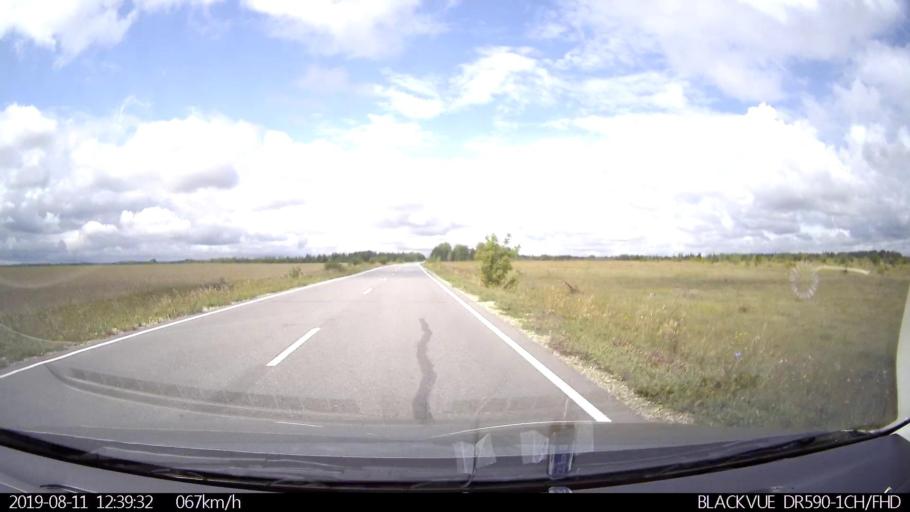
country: RU
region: Ulyanovsk
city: Ignatovka
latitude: 53.8337
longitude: 47.7942
